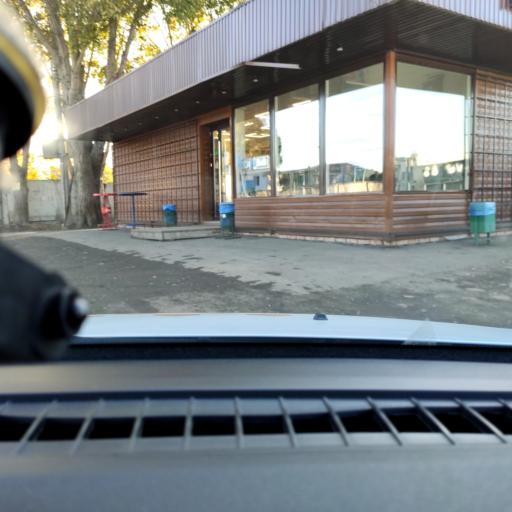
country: RU
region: Samara
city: Samara
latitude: 53.1937
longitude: 50.2737
